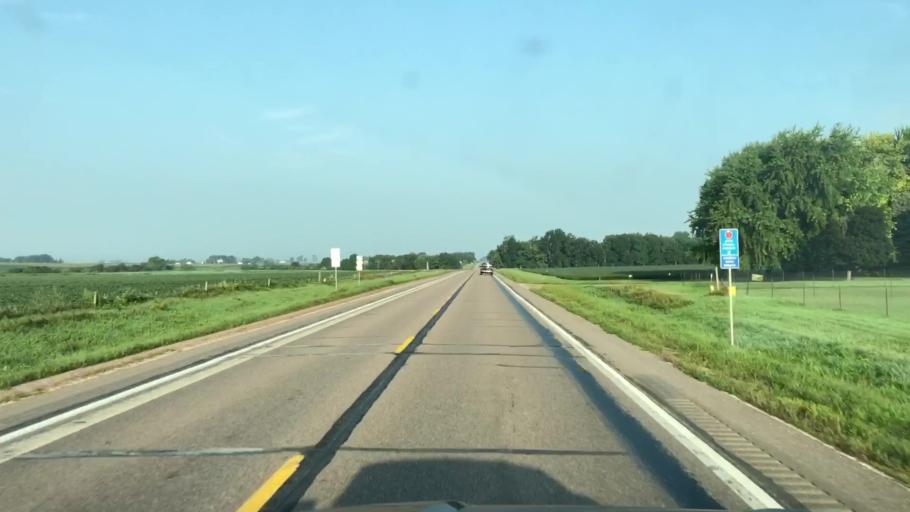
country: US
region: Iowa
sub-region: O'Brien County
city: Sheldon
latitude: 43.1860
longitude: -95.9228
